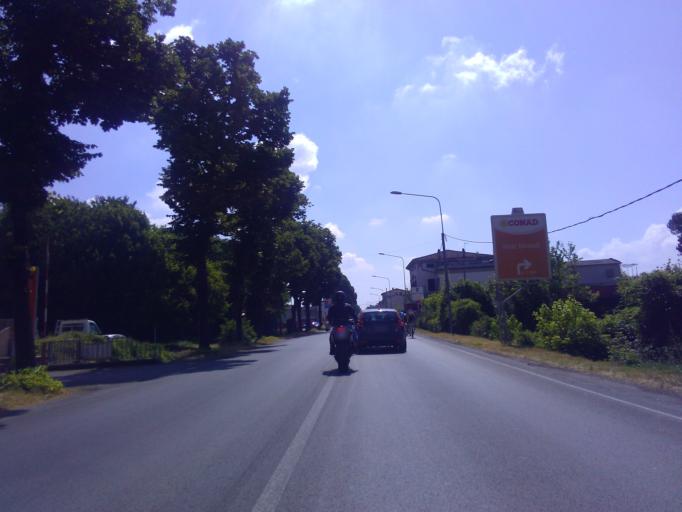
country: IT
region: Tuscany
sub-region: Provincia di Lucca
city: Lucca
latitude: 43.8502
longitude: 10.4595
